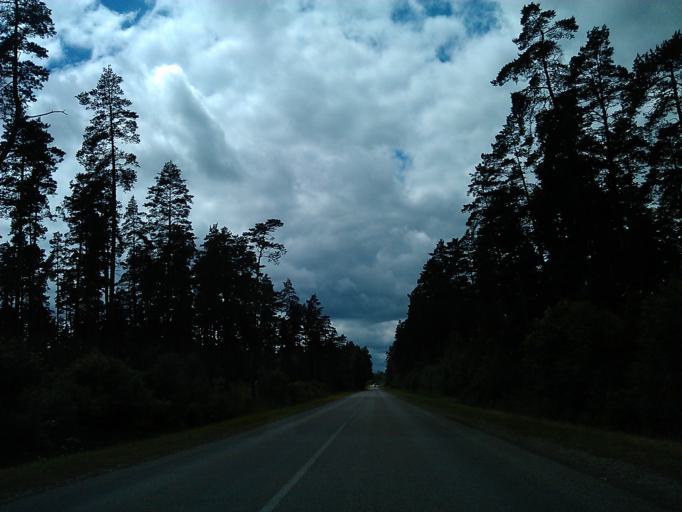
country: LV
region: Talsu Rajons
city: Stende
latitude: 57.0852
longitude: 22.3033
